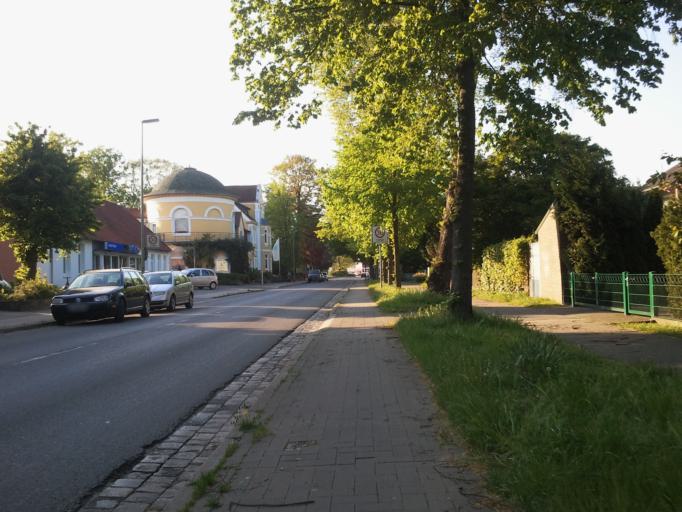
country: DE
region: Lower Saxony
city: Nienburg
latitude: 52.6330
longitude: 9.2150
